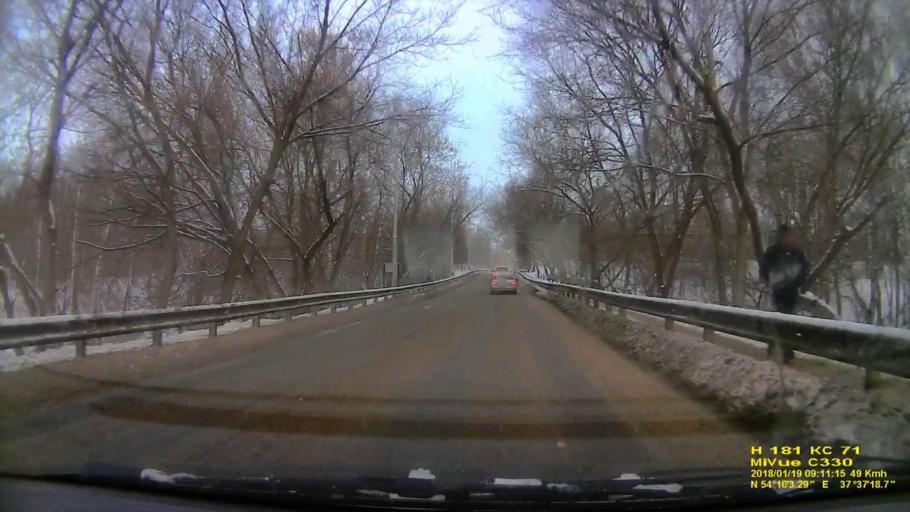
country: RU
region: Tula
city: Tula
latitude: 54.1655
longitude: 37.6212
